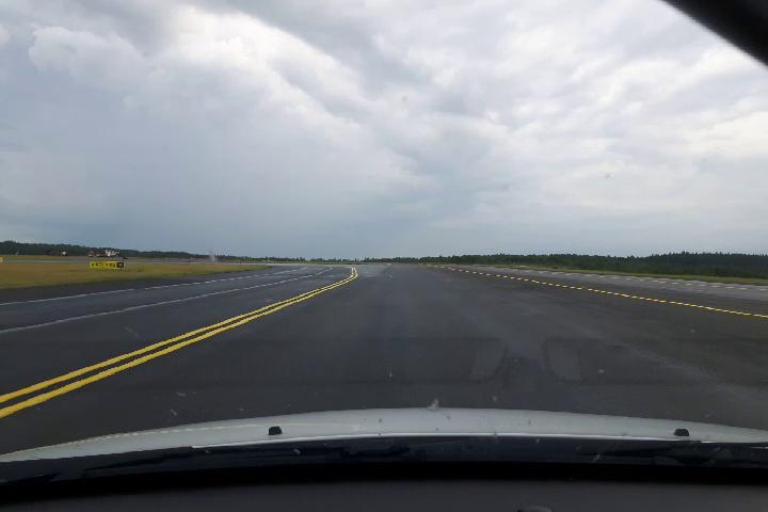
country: SE
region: Stockholm
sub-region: Sigtuna Kommun
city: Rosersberg
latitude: 59.6294
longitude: 17.9479
